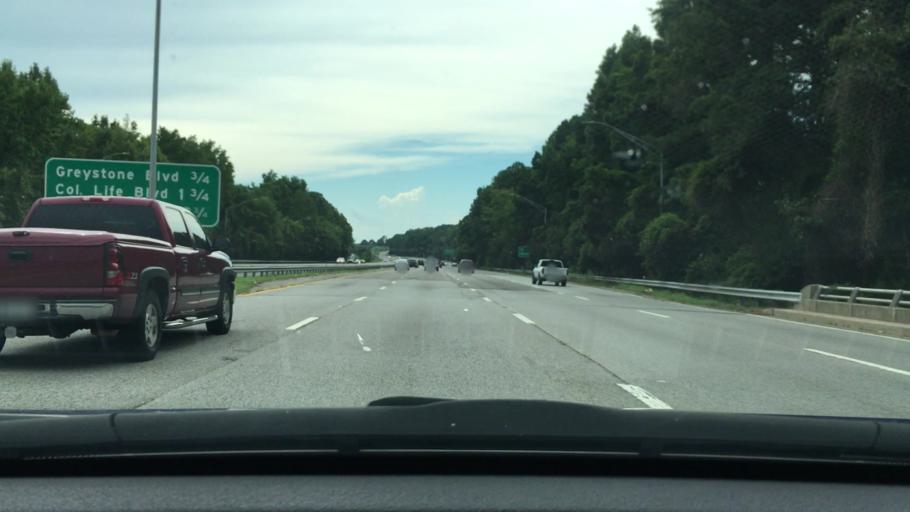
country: US
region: South Carolina
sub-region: Lexington County
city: West Columbia
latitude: 34.0101
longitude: -81.0623
